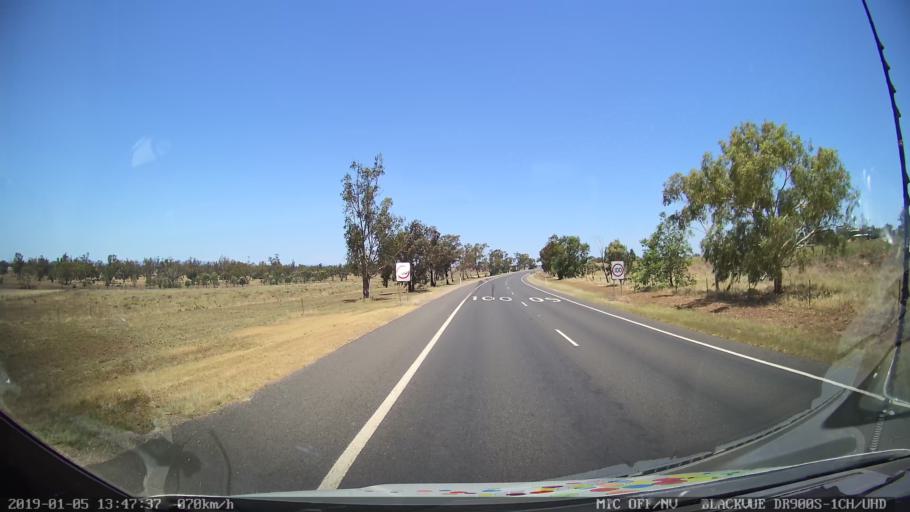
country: AU
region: New South Wales
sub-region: Gunnedah
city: Gunnedah
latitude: -30.9907
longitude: 150.2779
